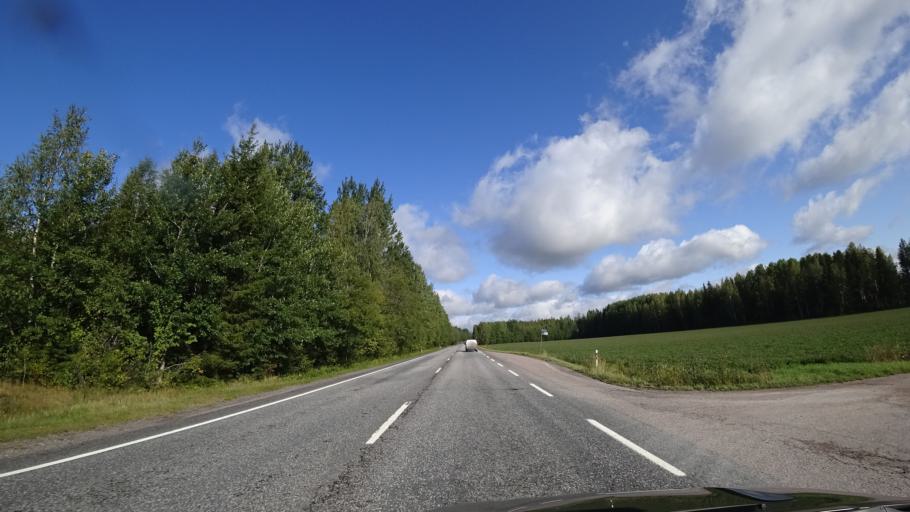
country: FI
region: Uusimaa
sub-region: Helsinki
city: Tuusula
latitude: 60.4716
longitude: 24.9429
